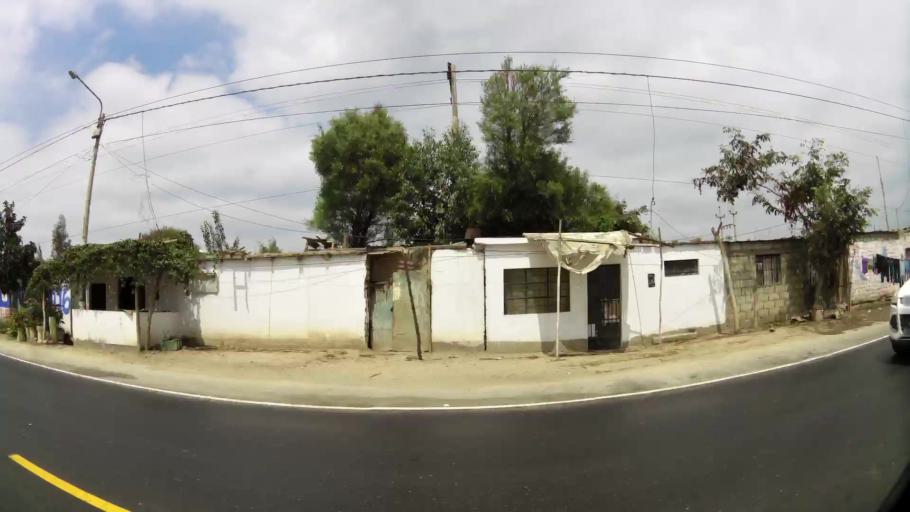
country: PE
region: La Libertad
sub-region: Ascope
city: Chocope
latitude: -7.7906
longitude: -79.2290
